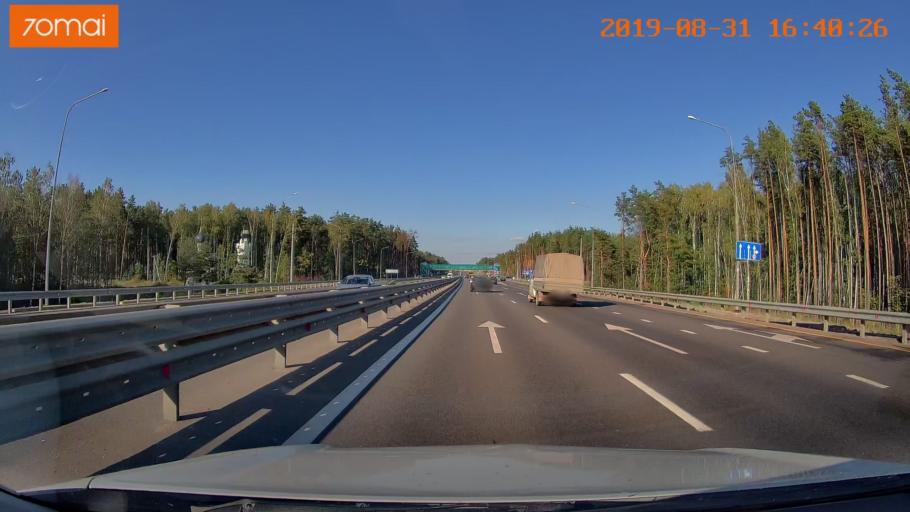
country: RU
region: Kaluga
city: Kurovskoye
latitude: 54.5654
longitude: 36.0487
